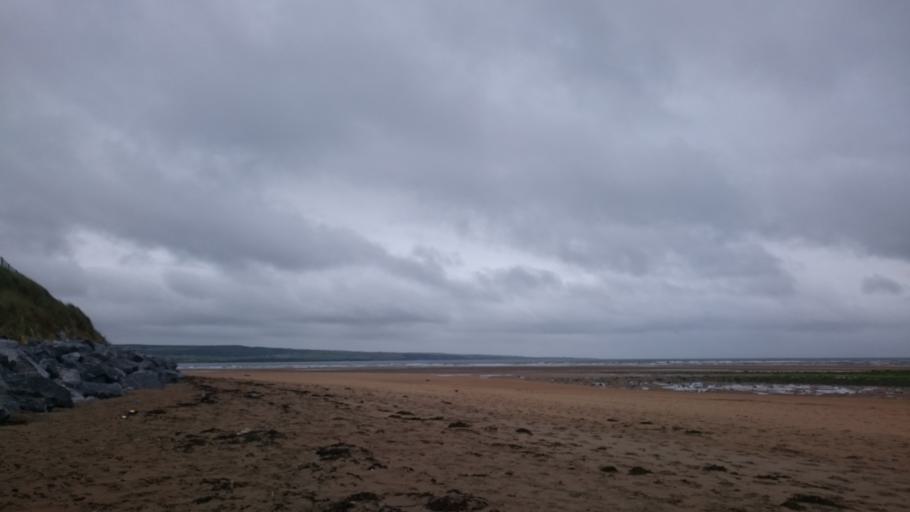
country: IE
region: Munster
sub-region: An Clar
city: Kilrush
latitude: 52.9426
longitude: -9.3585
